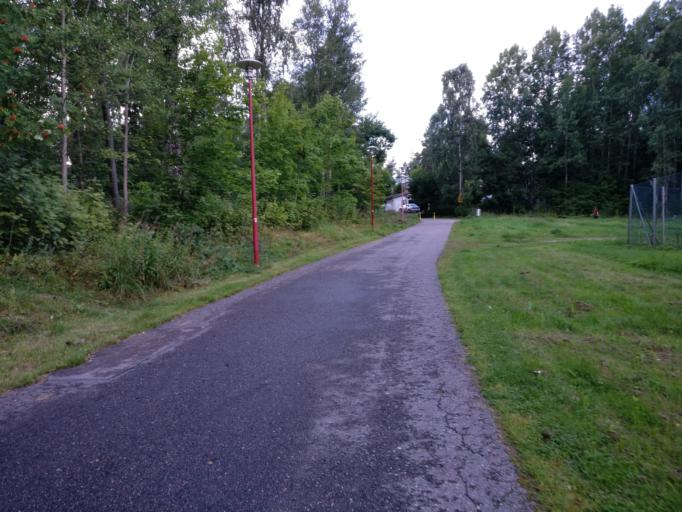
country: FI
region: Uusimaa
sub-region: Helsinki
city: Kilo
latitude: 60.2615
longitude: 24.8368
